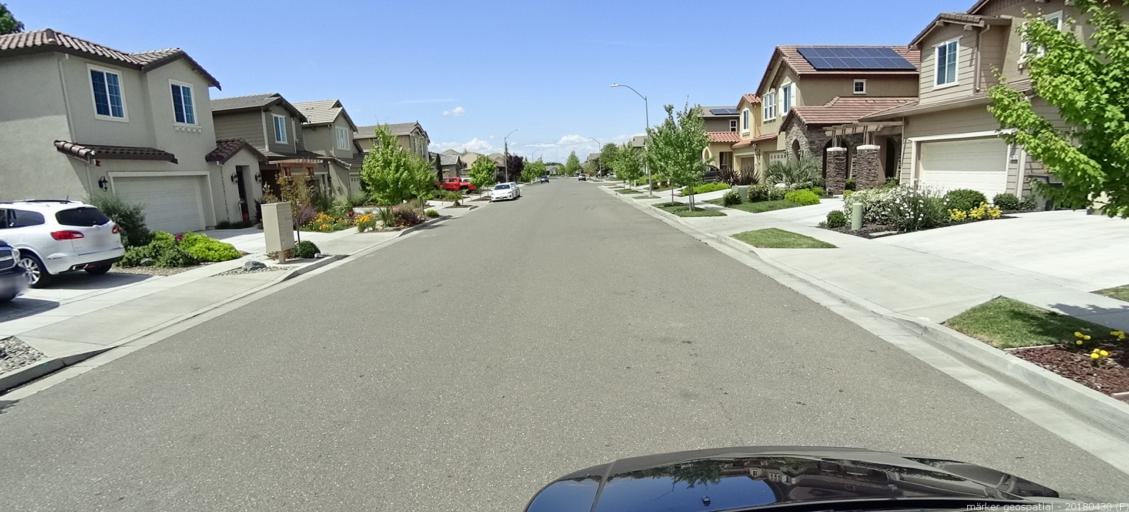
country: US
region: California
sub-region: Yolo County
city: West Sacramento
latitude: 38.5416
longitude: -121.5317
